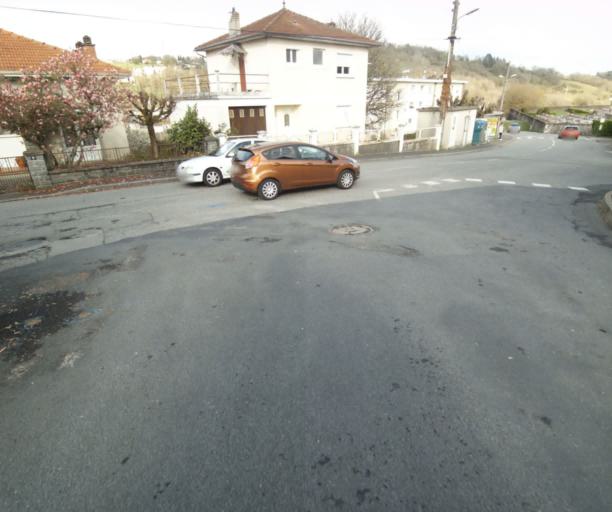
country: FR
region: Limousin
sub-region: Departement de la Correze
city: Tulle
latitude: 45.2543
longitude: 1.7557
